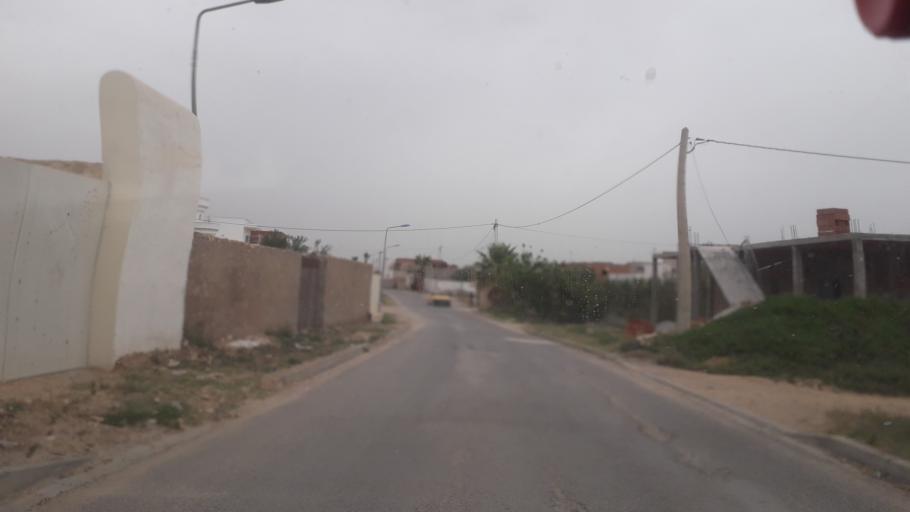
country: TN
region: Safaqis
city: Al Qarmadah
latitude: 34.7894
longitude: 10.7659
